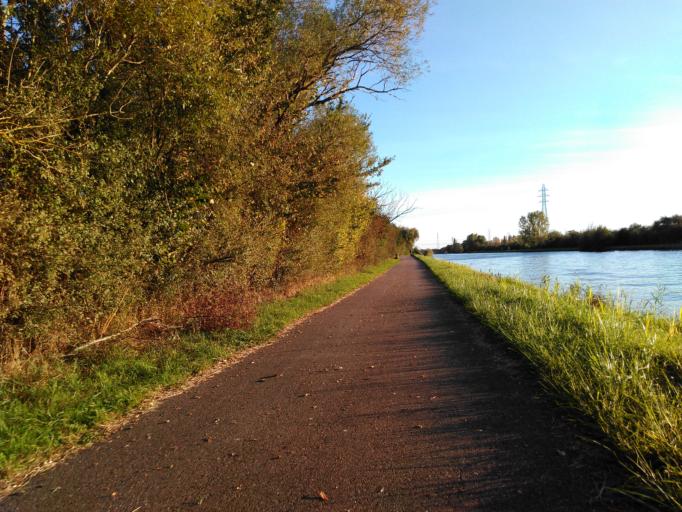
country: FR
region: Lorraine
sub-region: Departement de la Moselle
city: Maizieres-les-Metz
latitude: 49.2135
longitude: 6.1820
